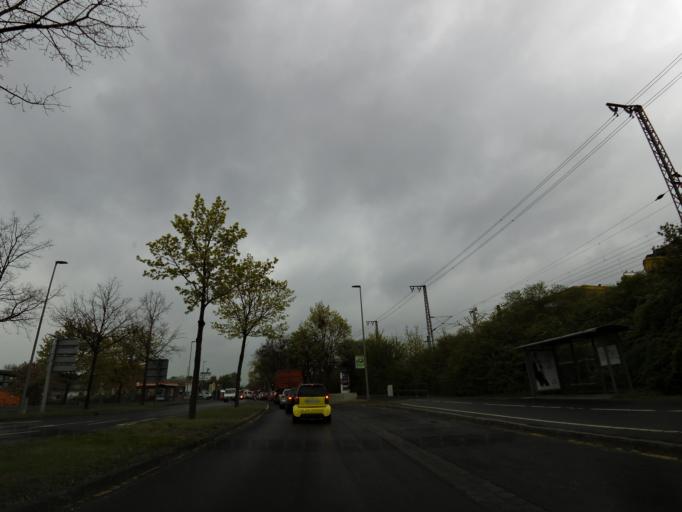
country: DE
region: Lower Saxony
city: Goettingen
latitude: 51.5417
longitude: 9.9276
